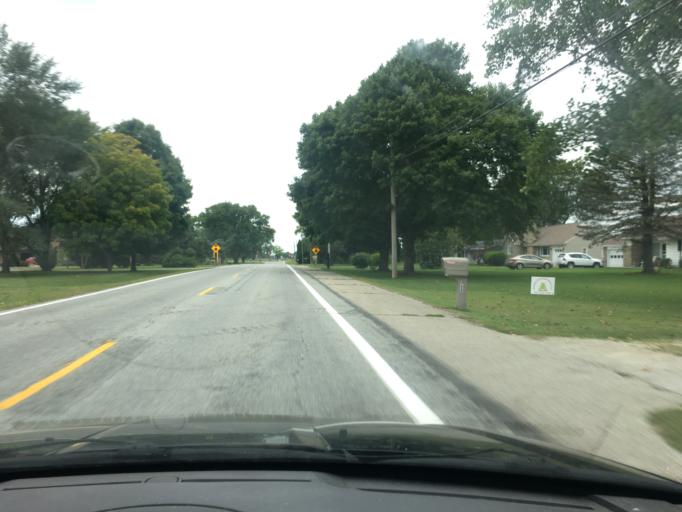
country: US
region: Ohio
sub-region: Champaign County
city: Urbana
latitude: 40.1551
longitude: -83.7426
